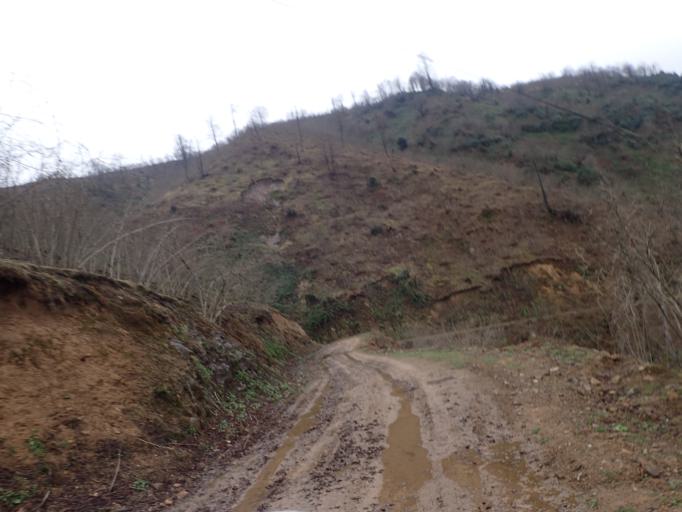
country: TR
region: Ordu
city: Camas
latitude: 40.8583
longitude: 37.5155
